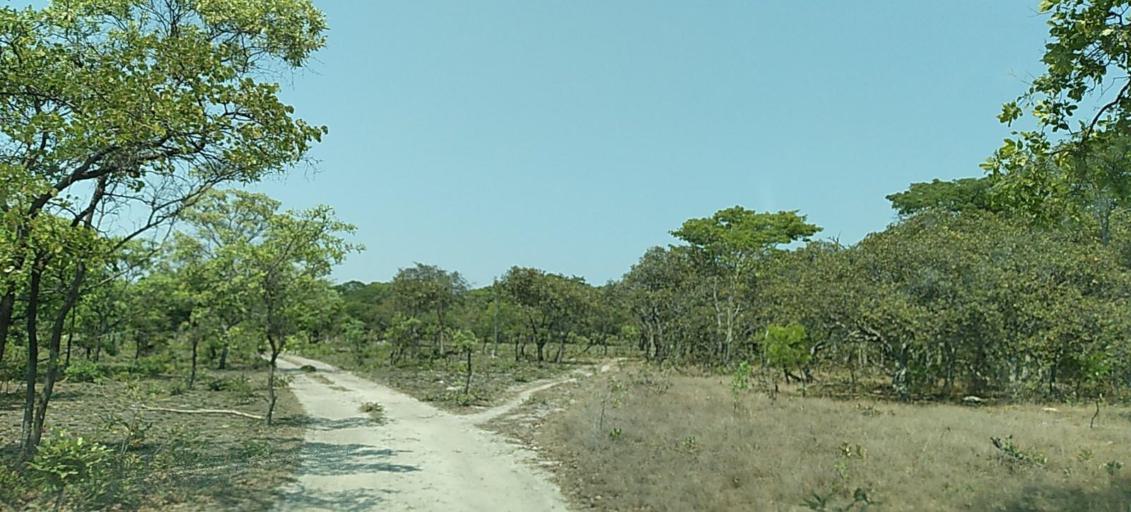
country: ZM
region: Copperbelt
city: Mpongwe
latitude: -13.8445
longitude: 28.0566
